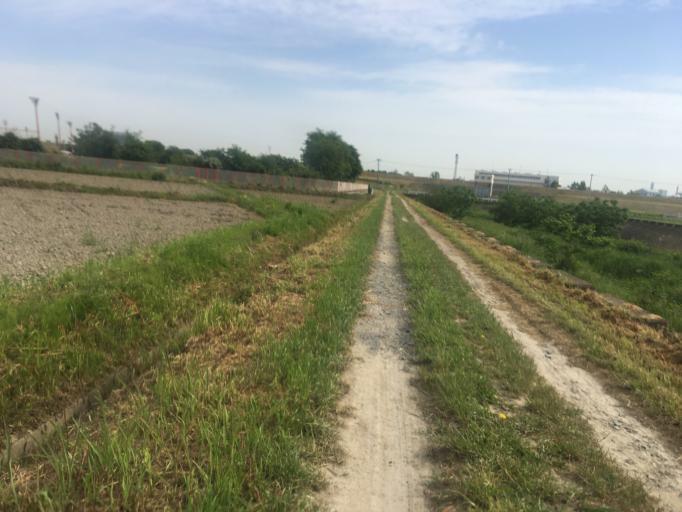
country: JP
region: Saitama
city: Shiki
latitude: 35.8529
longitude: 139.6031
